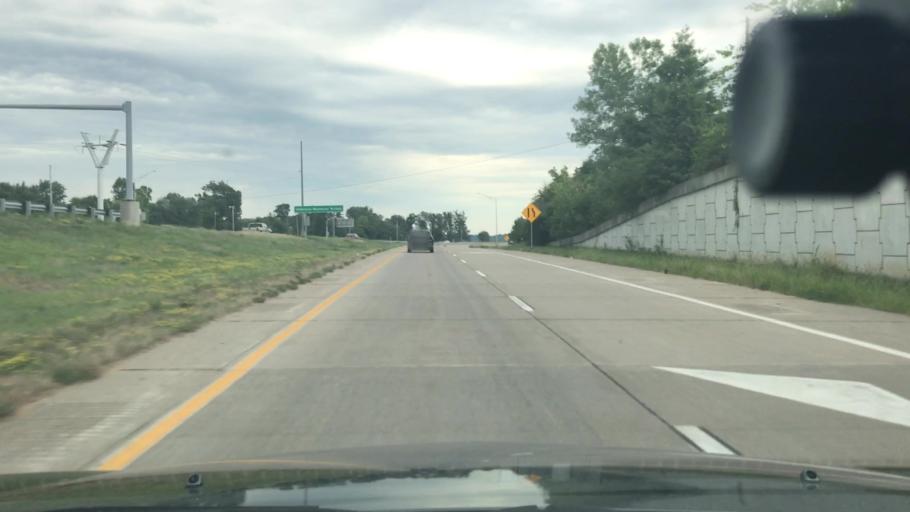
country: US
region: Missouri
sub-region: Saint Charles County
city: Saint Charles
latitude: 38.7423
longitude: -90.5283
